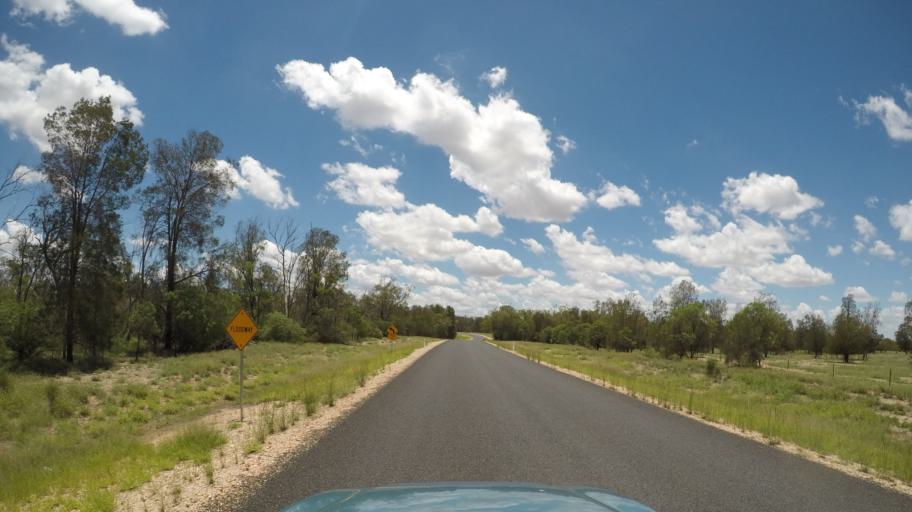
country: AU
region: Queensland
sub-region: Goondiwindi
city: Goondiwindi
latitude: -28.1512
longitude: 150.1260
